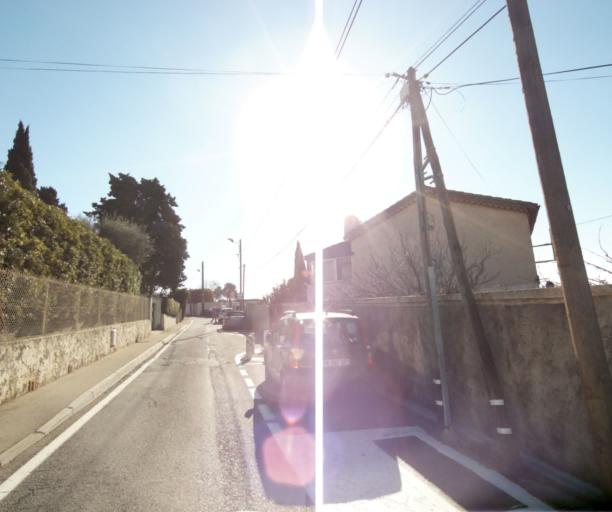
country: FR
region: Provence-Alpes-Cote d'Azur
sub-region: Departement des Alpes-Maritimes
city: Biot
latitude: 43.6051
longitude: 7.0844
